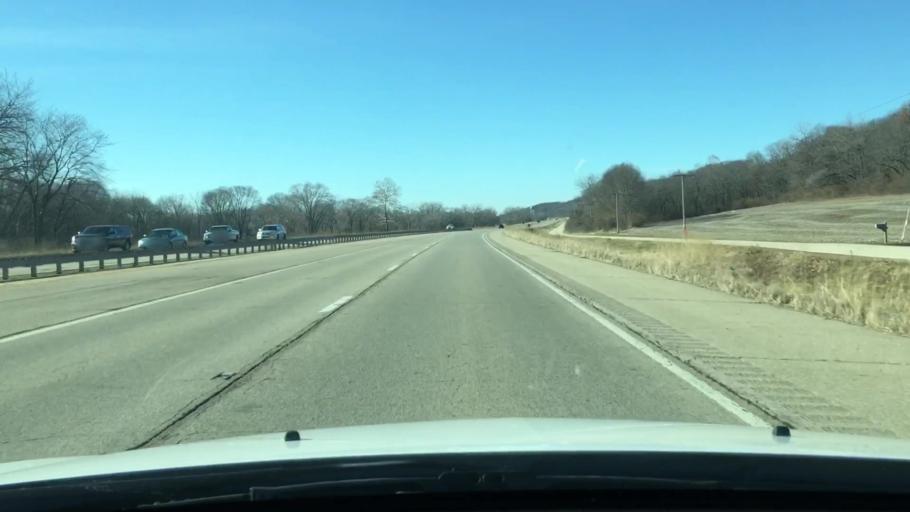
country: US
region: Illinois
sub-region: Peoria County
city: Glasford
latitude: 40.5610
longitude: -89.7537
